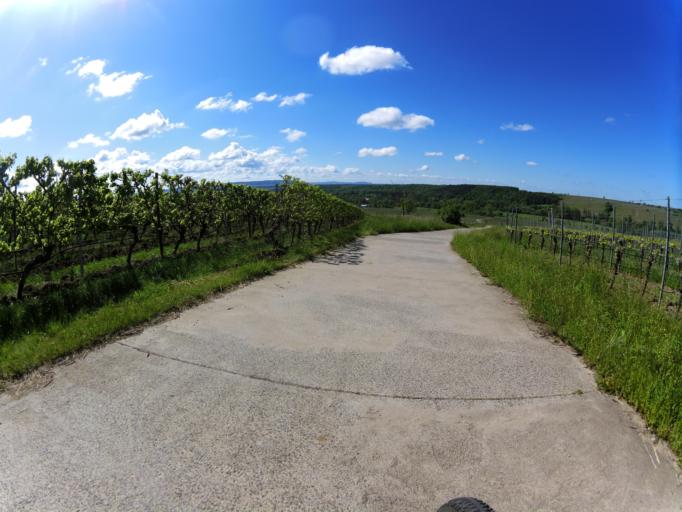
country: DE
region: Bavaria
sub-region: Regierungsbezirk Unterfranken
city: Sommerach
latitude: 49.8370
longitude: 10.1987
